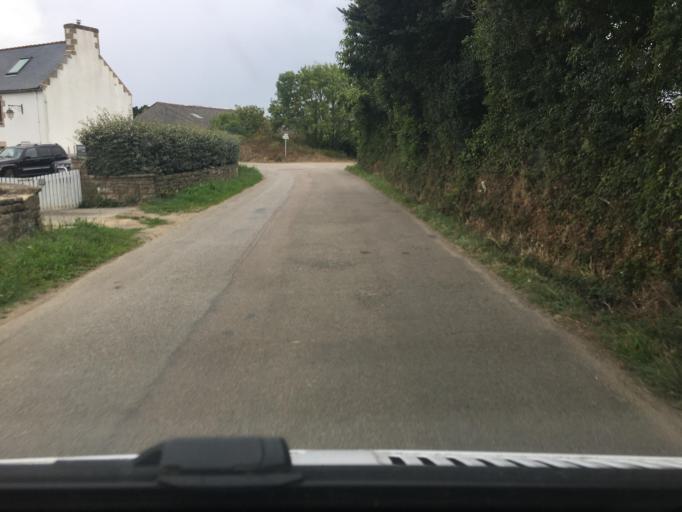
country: FR
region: Brittany
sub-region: Departement du Finistere
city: Beuzec-Cap-Sizun
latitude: 48.0832
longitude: -4.4772
